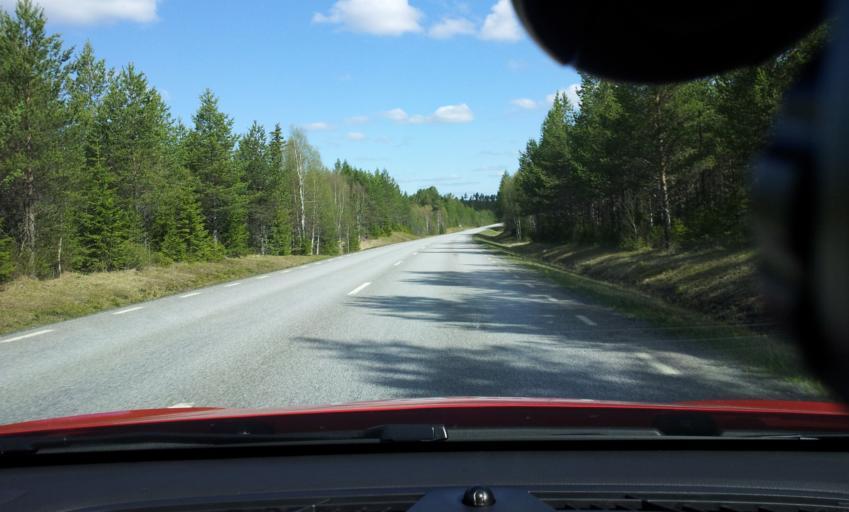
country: SE
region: Jaemtland
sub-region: Krokoms Kommun
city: Valla
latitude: 63.2885
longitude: 13.9276
